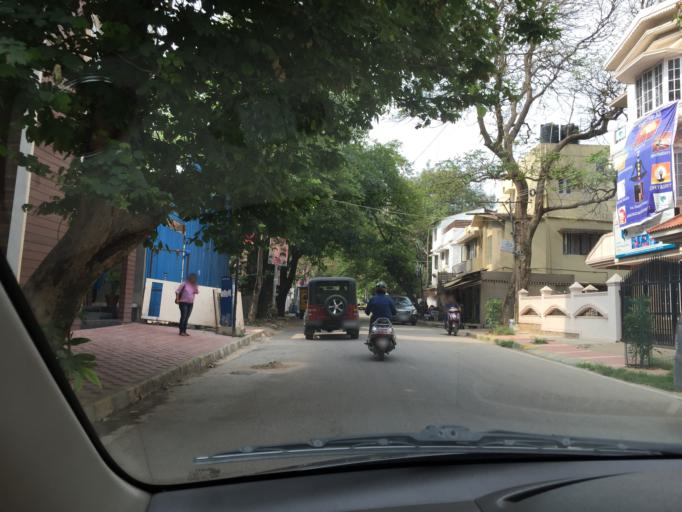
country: IN
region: Karnataka
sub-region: Bangalore Urban
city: Bangalore
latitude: 13.0008
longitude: 77.6234
